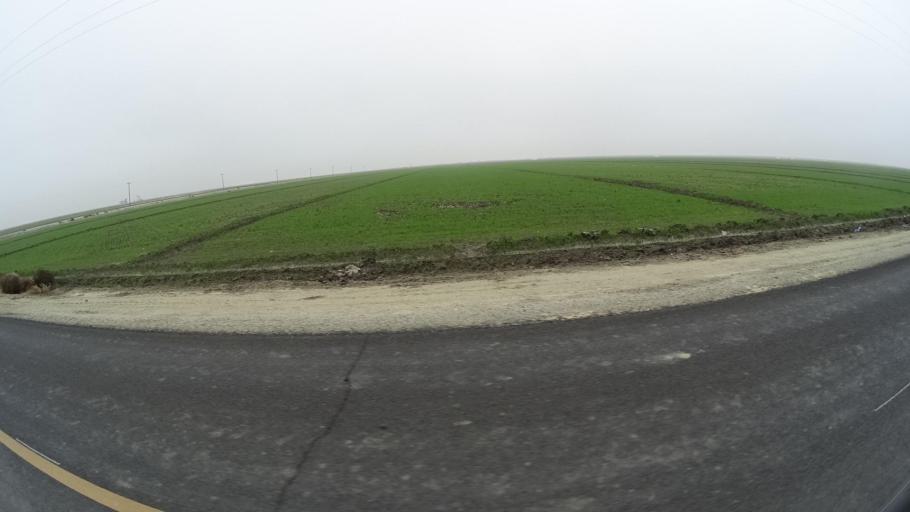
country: US
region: California
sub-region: Kern County
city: Greenfield
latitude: 35.1801
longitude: -119.1801
